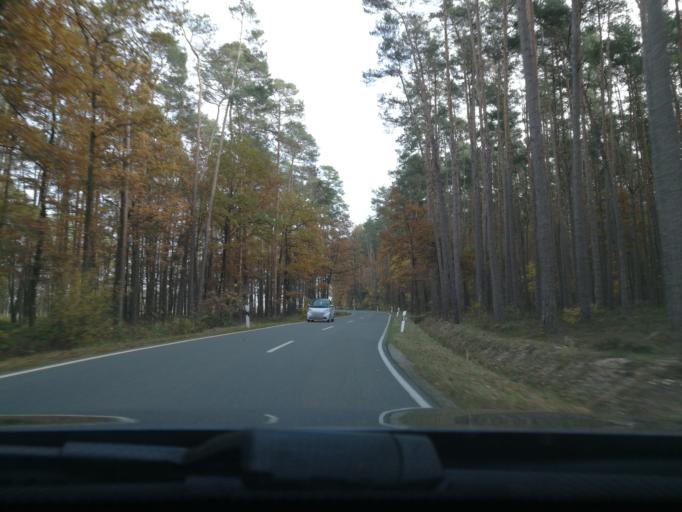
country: DE
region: Bavaria
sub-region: Regierungsbezirk Mittelfranken
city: Puschendorf
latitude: 49.5624
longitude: 10.8372
